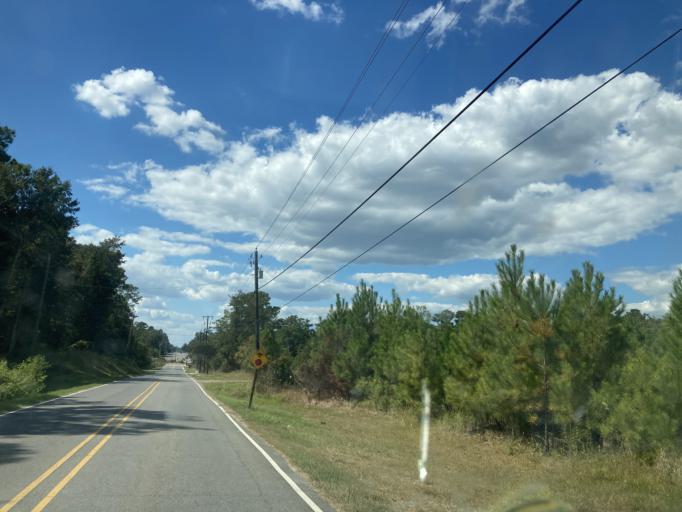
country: US
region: Mississippi
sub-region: Jackson County
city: Gulf Hills
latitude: 30.4433
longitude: -88.8398
